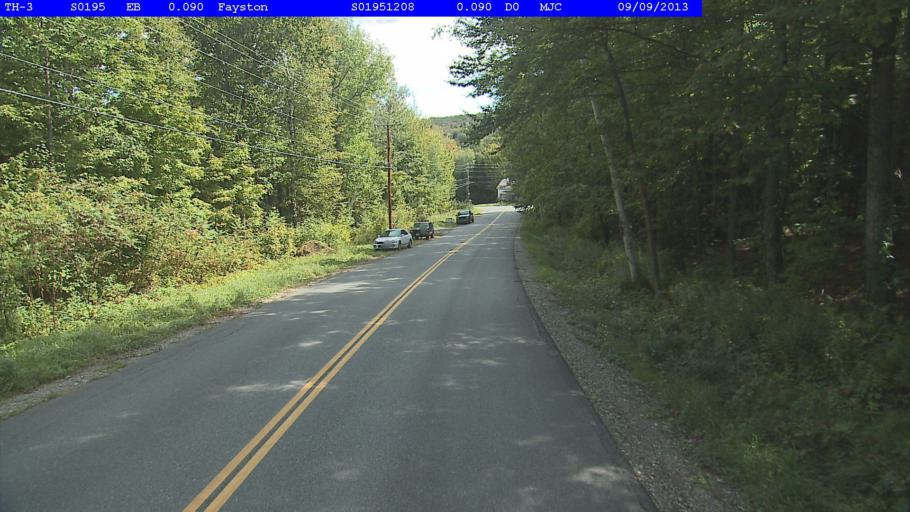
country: US
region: Vermont
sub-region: Addison County
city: Bristol
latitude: 44.1777
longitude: -72.8908
